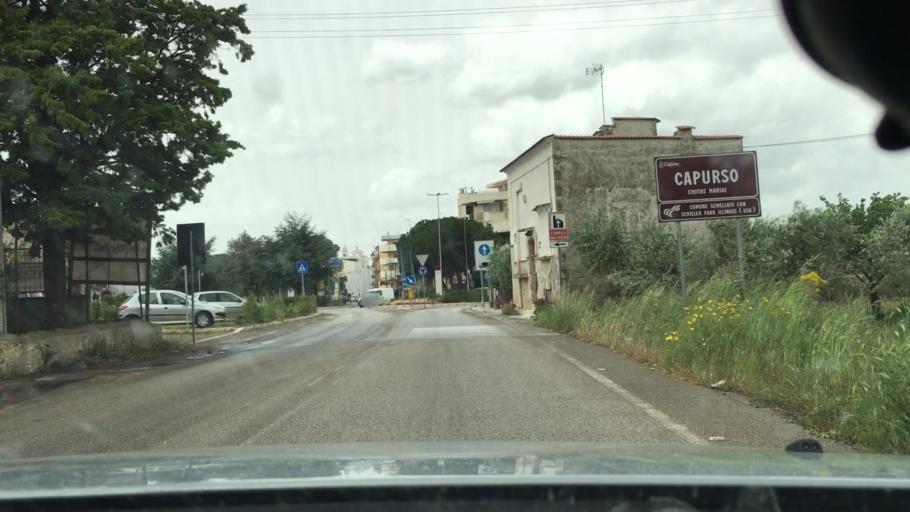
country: IT
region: Apulia
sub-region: Provincia di Bari
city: Capurso
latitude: 41.0446
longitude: 16.9307
